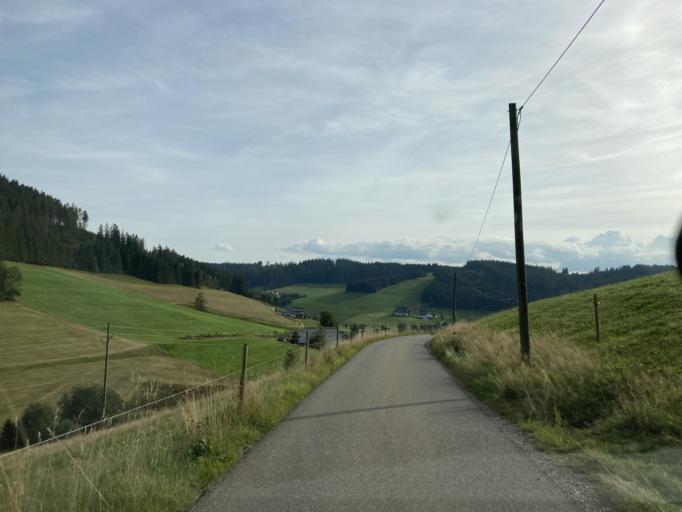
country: DE
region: Baden-Wuerttemberg
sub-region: Freiburg Region
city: Titisee-Neustadt
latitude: 47.9866
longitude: 8.1783
